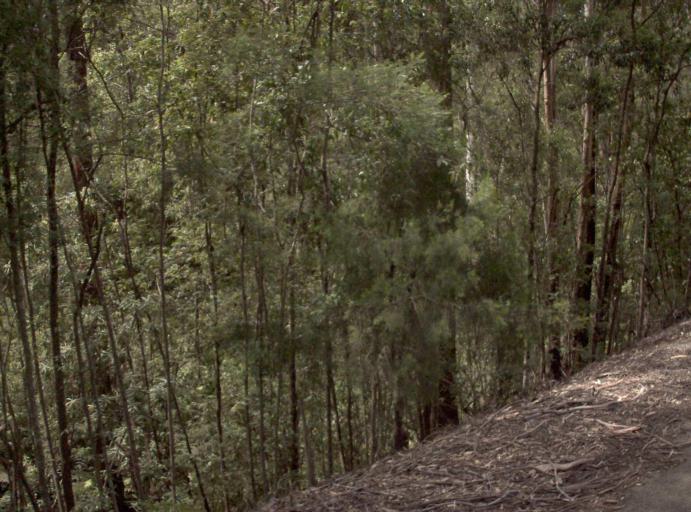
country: AU
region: New South Wales
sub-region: Bombala
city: Bombala
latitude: -37.5356
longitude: 149.3716
